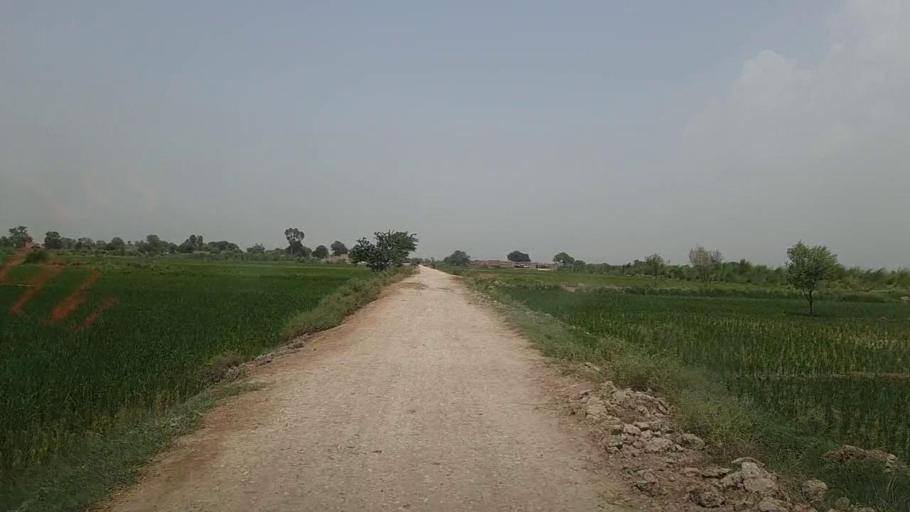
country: PK
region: Sindh
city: Sita Road
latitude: 27.0794
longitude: 67.8723
